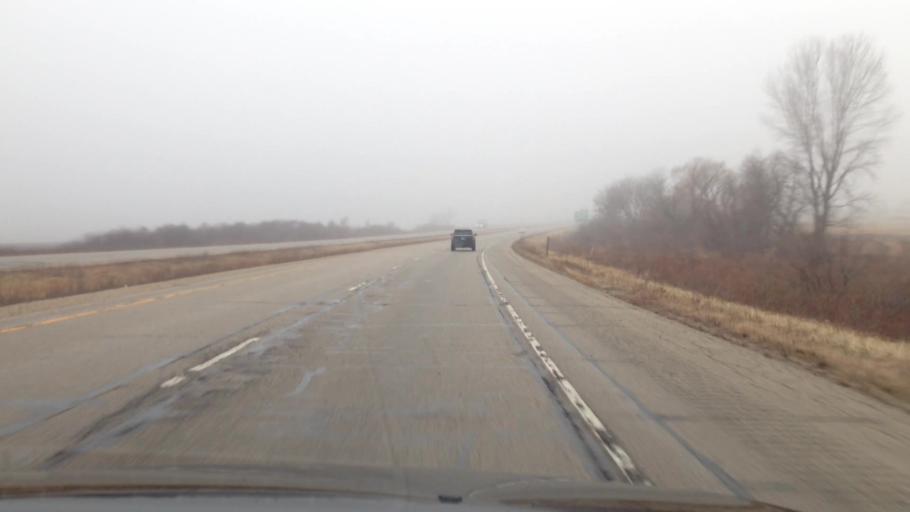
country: US
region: Wisconsin
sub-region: Walworth County
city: Como
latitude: 42.6467
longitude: -88.5025
